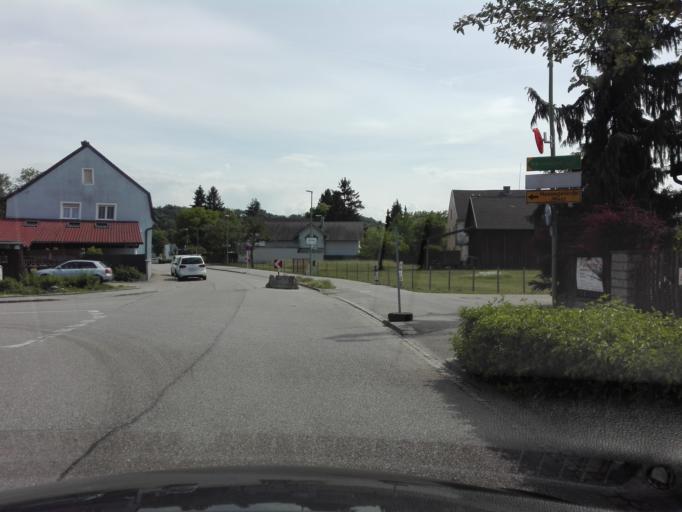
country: AT
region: Upper Austria
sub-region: Wels-Land
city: Thalheim bei Wels
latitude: 48.1500
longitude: 14.0101
